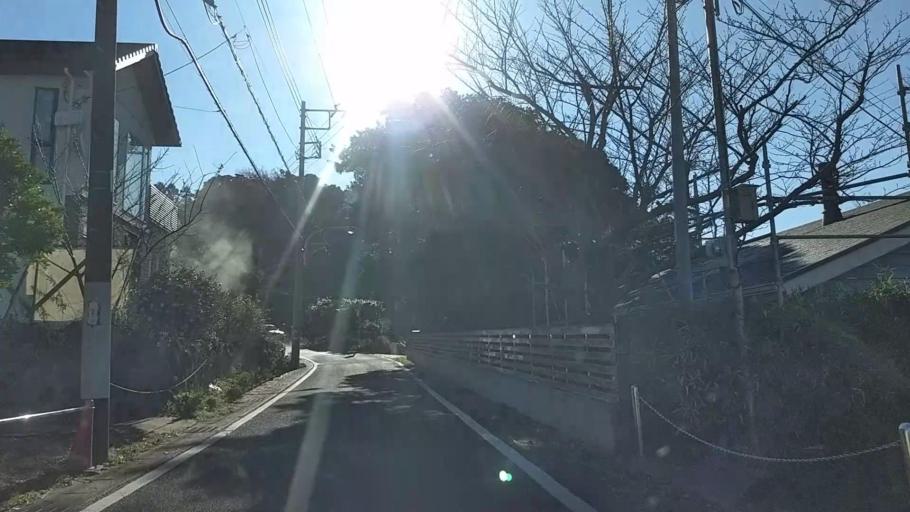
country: JP
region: Chiba
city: Futtsu
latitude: 35.2443
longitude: 139.8695
